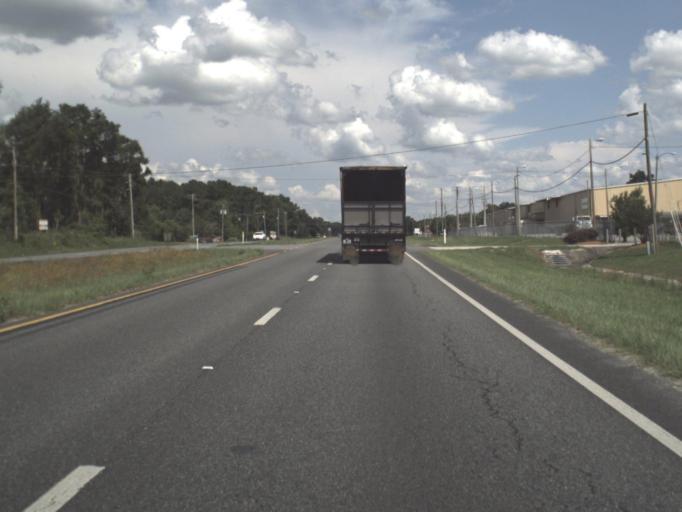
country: US
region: Florida
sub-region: Alachua County
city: High Springs
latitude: 29.8213
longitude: -82.5840
